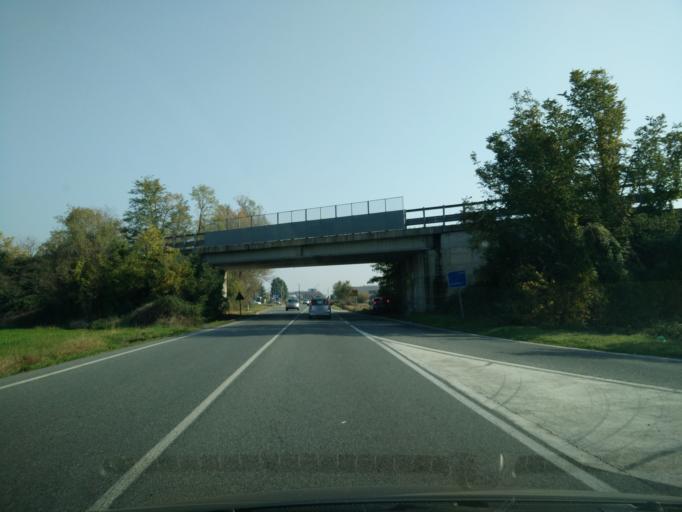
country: IT
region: Piedmont
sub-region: Provincia di Torino
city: Leini
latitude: 45.1822
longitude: 7.6887
